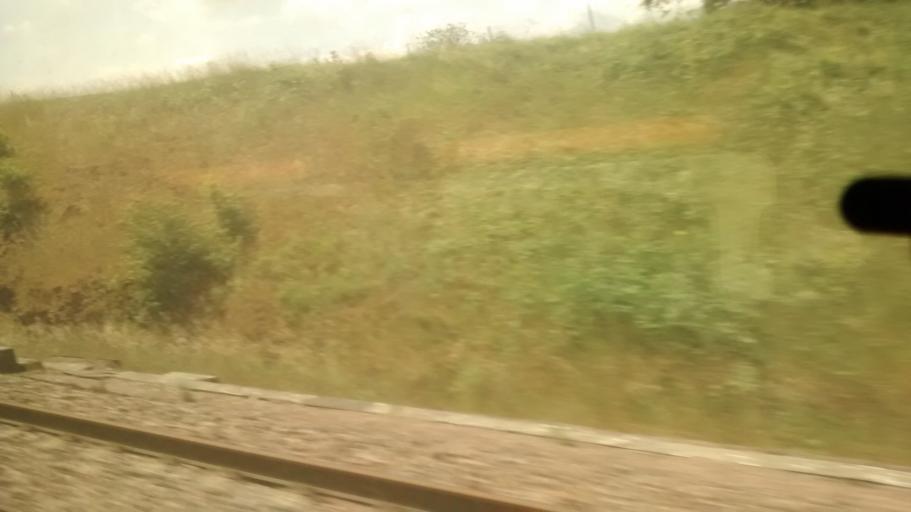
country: FR
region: Bourgogne
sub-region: Departement de Saone-et-Loire
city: Ecuisses
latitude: 46.6820
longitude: 4.5680
